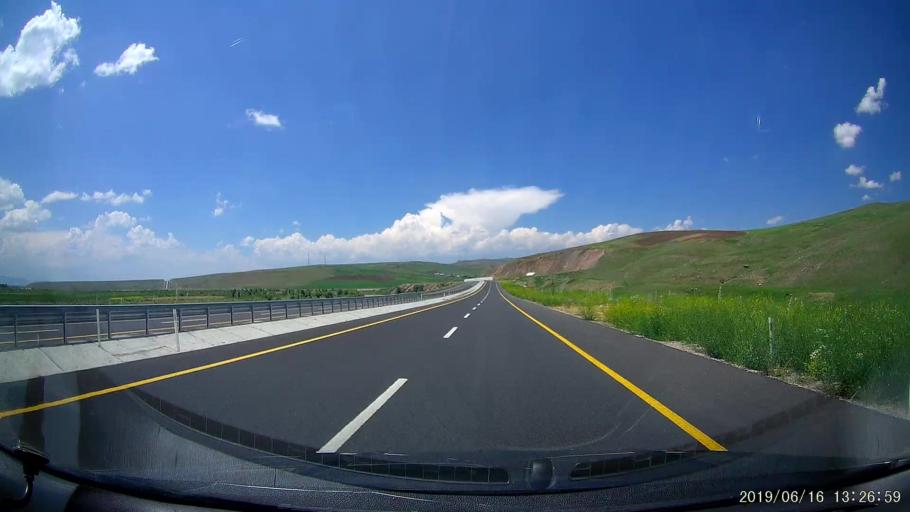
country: TR
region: Agri
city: Taslicay
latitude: 39.6649
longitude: 43.3176
